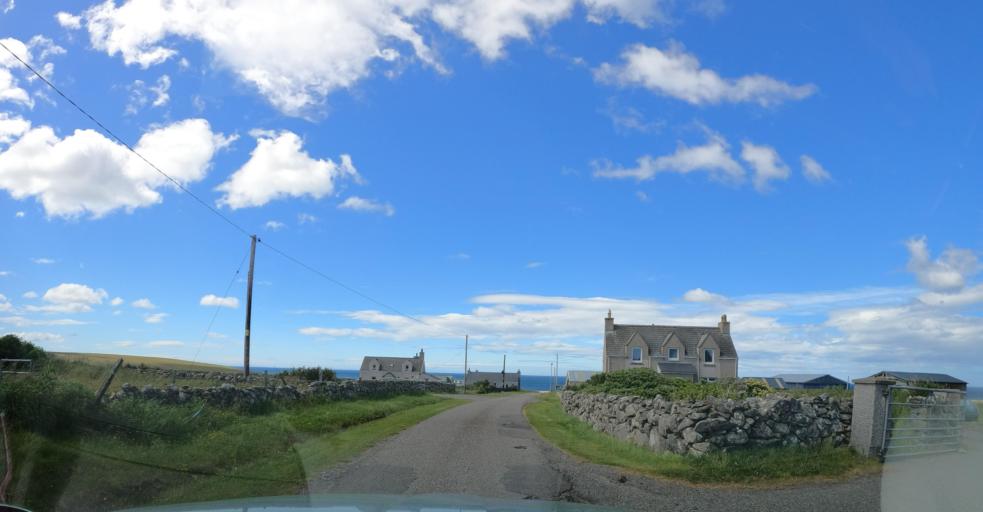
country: GB
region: Scotland
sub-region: Eilean Siar
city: Isle of Lewis
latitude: 58.3594
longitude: -6.5609
